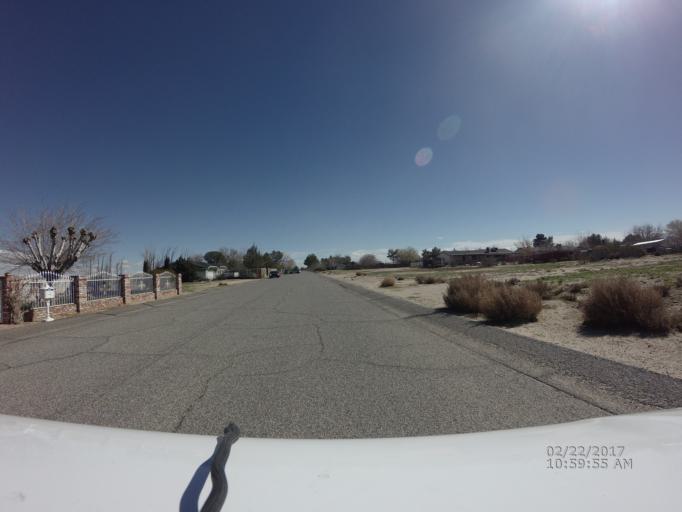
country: US
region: California
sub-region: Los Angeles County
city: Lake Los Angeles
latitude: 34.6302
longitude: -117.8160
